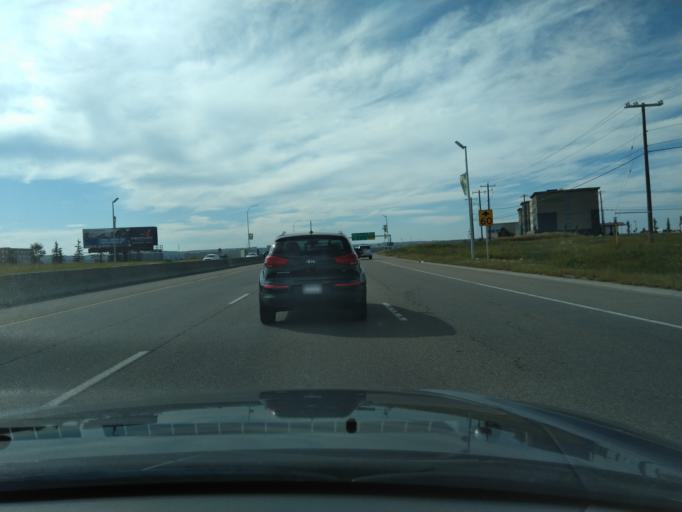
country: CA
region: Alberta
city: Calgary
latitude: 51.1394
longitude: -114.0231
